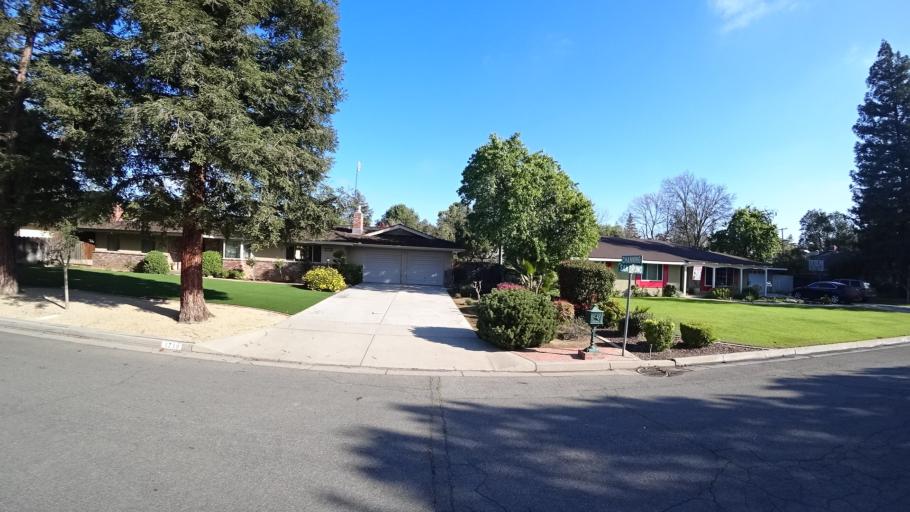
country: US
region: California
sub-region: Fresno County
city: Fresno
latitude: 36.8128
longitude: -119.8242
